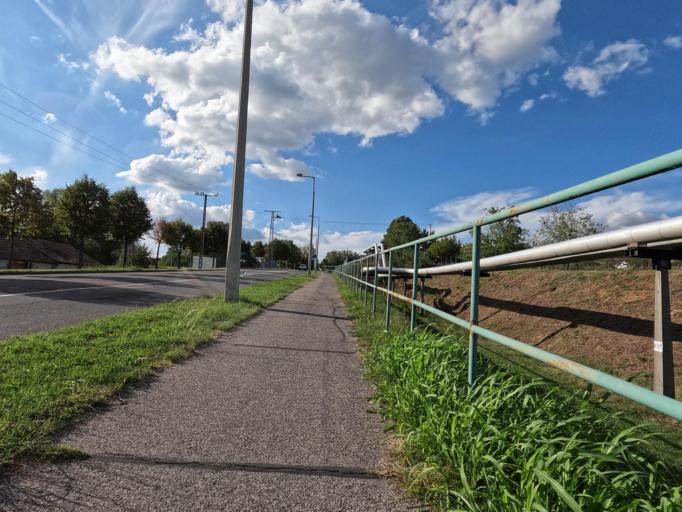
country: HU
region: Tolna
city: Paks
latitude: 46.6092
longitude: 18.8410
